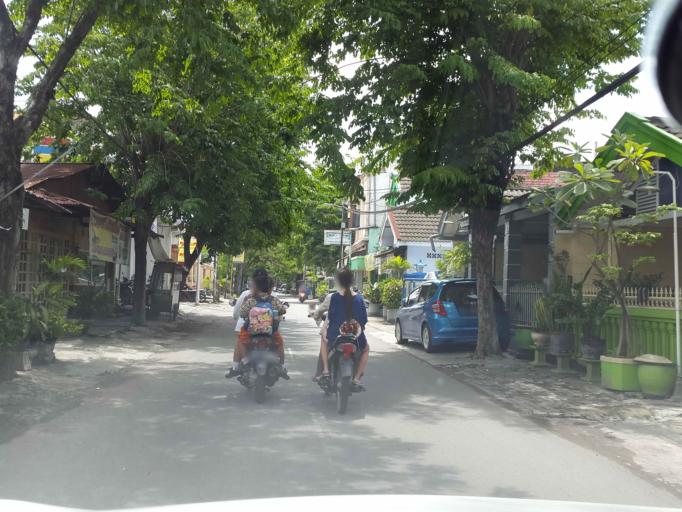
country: ID
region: East Java
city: Mojokerto
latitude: -7.4578
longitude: 112.4486
